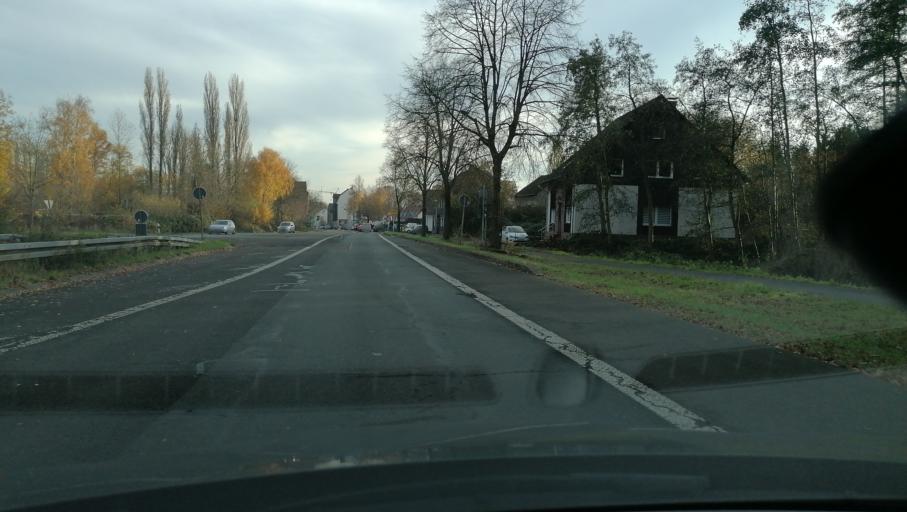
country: DE
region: North Rhine-Westphalia
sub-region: Regierungsbezirk Arnsberg
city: Dortmund
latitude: 51.5433
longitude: 7.4069
